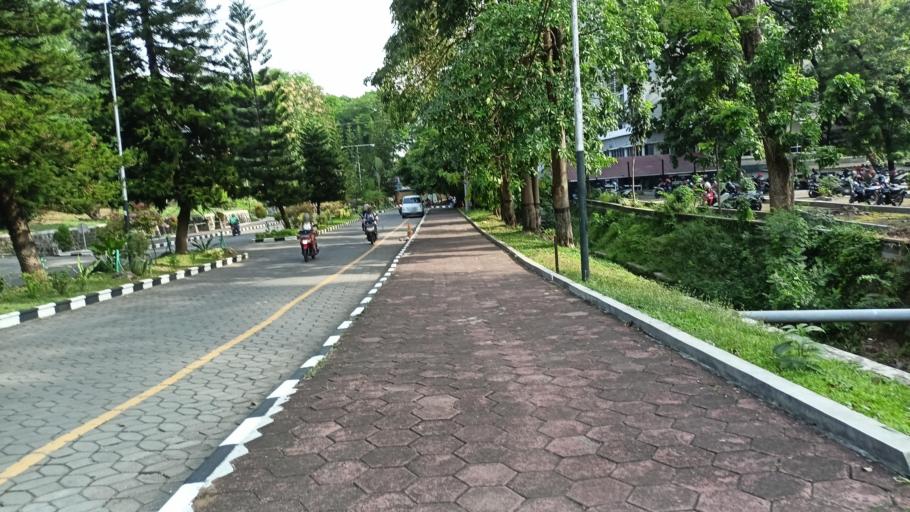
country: ID
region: Central Java
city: Surakarta
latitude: -7.5564
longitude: 110.8569
